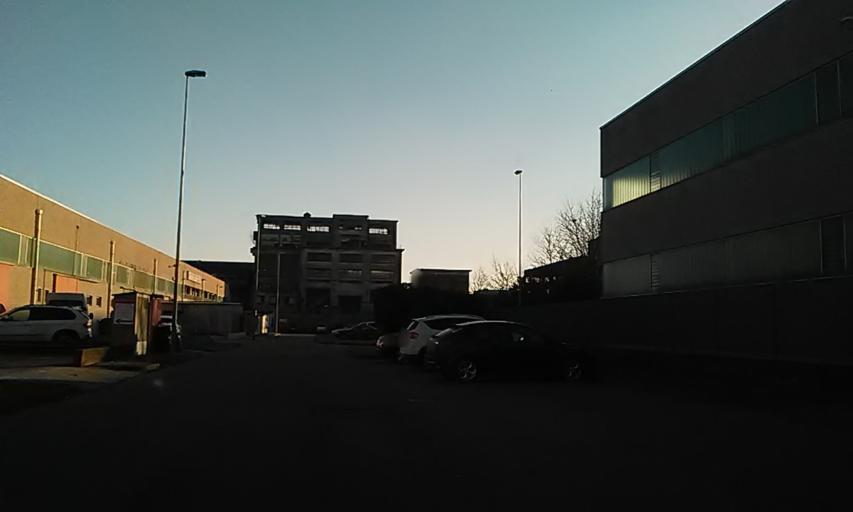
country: IT
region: Piedmont
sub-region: Provincia di Vercelli
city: Vercelli
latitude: 45.3351
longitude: 8.4330
